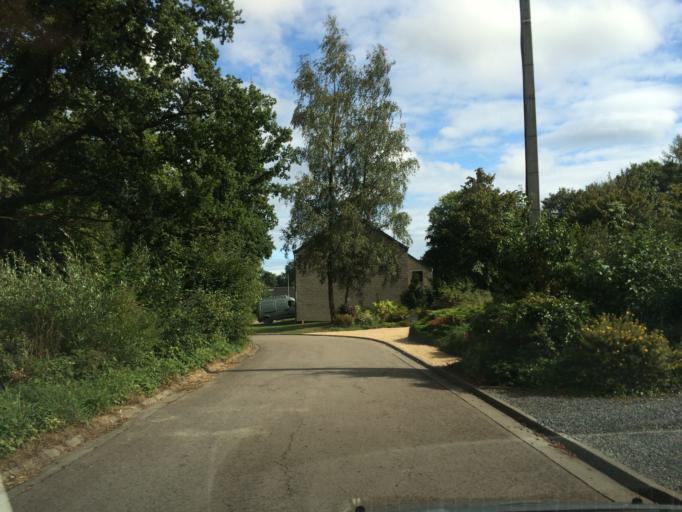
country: BE
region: Wallonia
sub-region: Province du Luxembourg
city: Chiny
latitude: 49.7004
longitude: 5.3742
